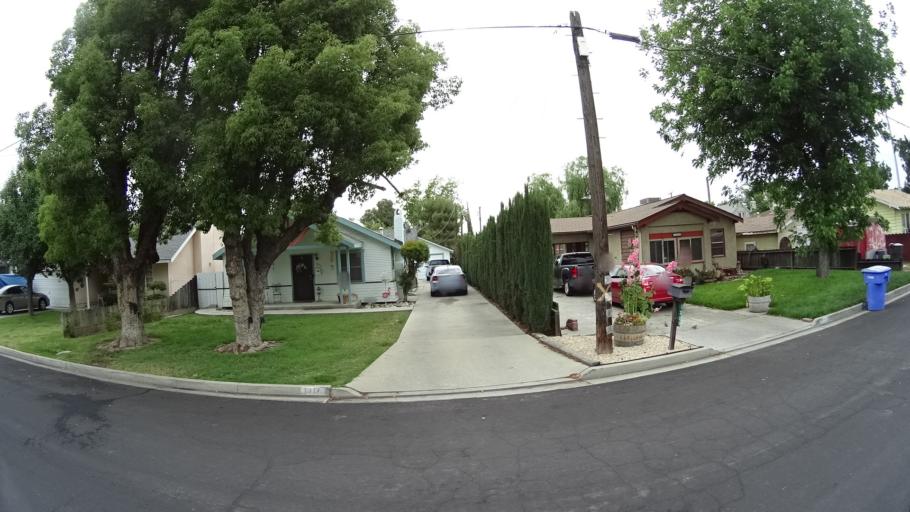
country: US
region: California
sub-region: Kings County
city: Hanford
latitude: 36.3395
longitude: -119.6537
